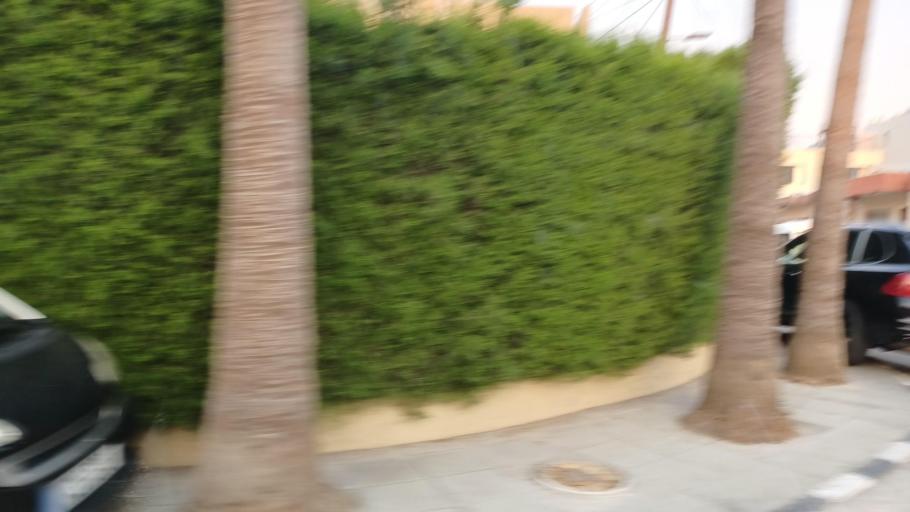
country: CY
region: Limassol
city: Pano Polemidia
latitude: 34.6854
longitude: 33.0046
